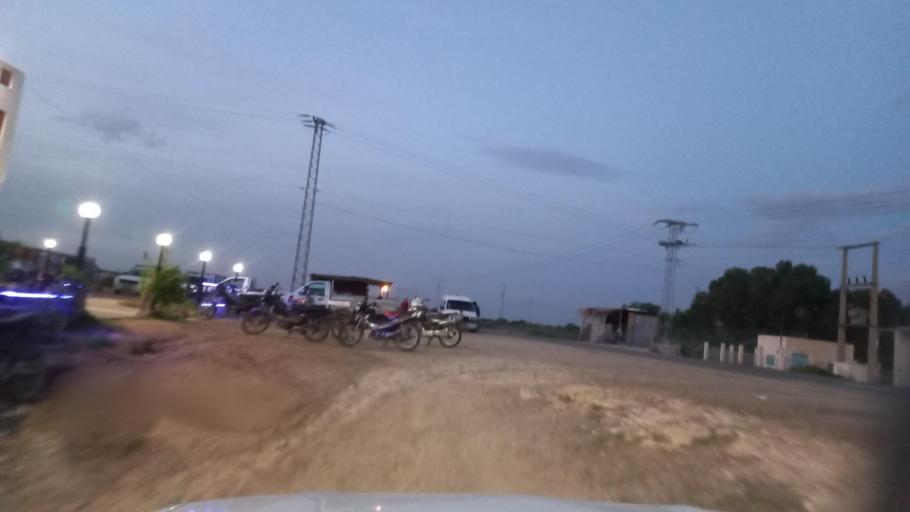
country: TN
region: Al Qasrayn
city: Sbiba
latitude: 35.4162
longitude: 9.1253
